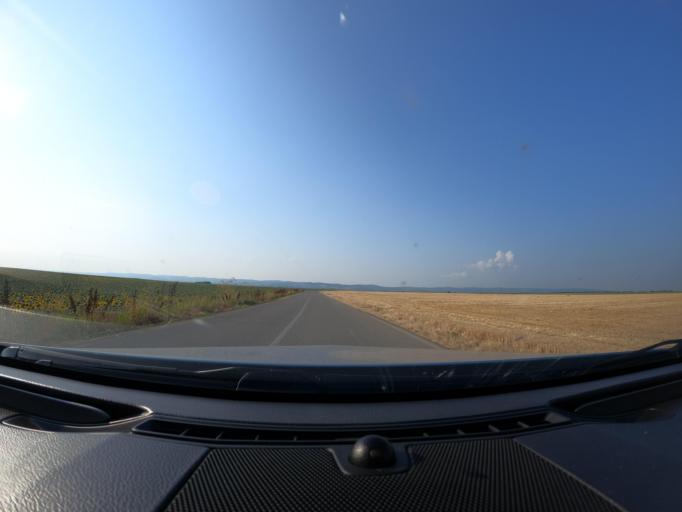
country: RS
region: Autonomna Pokrajina Vojvodina
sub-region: Sremski Okrug
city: Ruma
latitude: 45.0334
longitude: 19.7621
